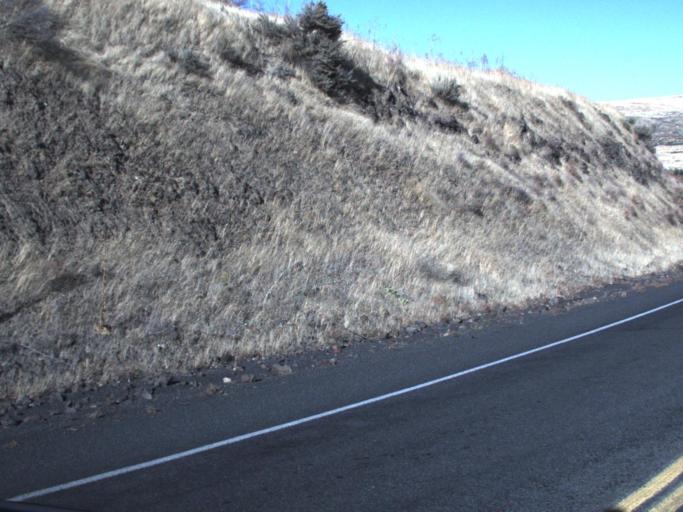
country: US
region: Washington
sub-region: Franklin County
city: Connell
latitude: 46.6359
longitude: -118.5560
